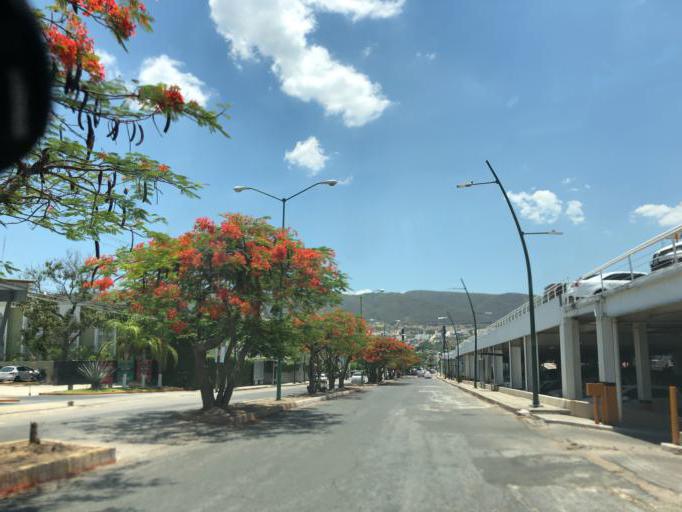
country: MX
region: Chiapas
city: Tuxtla Gutierrez
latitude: 16.7532
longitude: -93.1508
